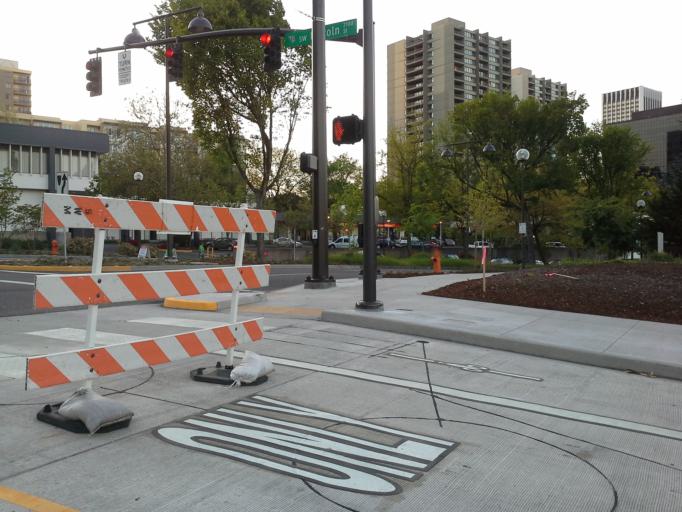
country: US
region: Oregon
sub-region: Multnomah County
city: Portland
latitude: 45.5080
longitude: -122.6785
